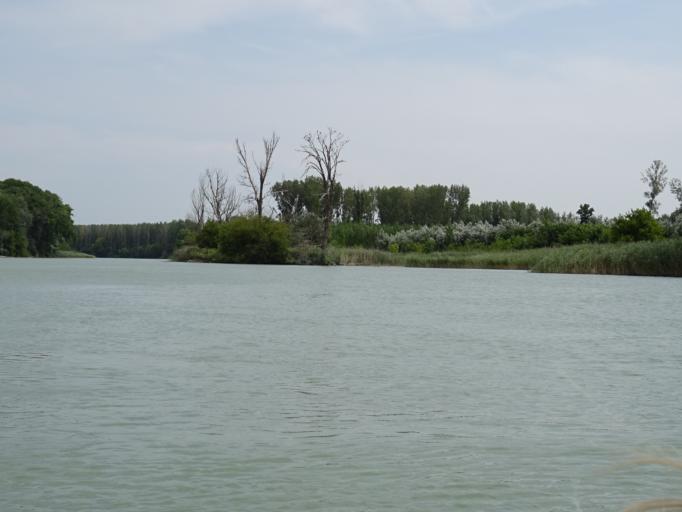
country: HU
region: Gyor-Moson-Sopron
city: Halaszi
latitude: 47.9423
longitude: 17.3905
